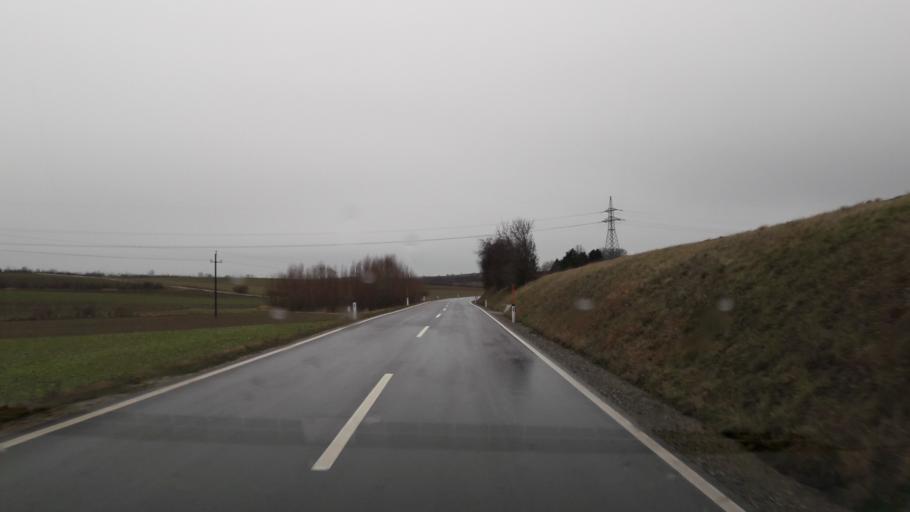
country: AT
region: Lower Austria
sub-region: Politischer Bezirk Mistelbach
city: Hochleithen
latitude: 48.4340
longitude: 16.5447
